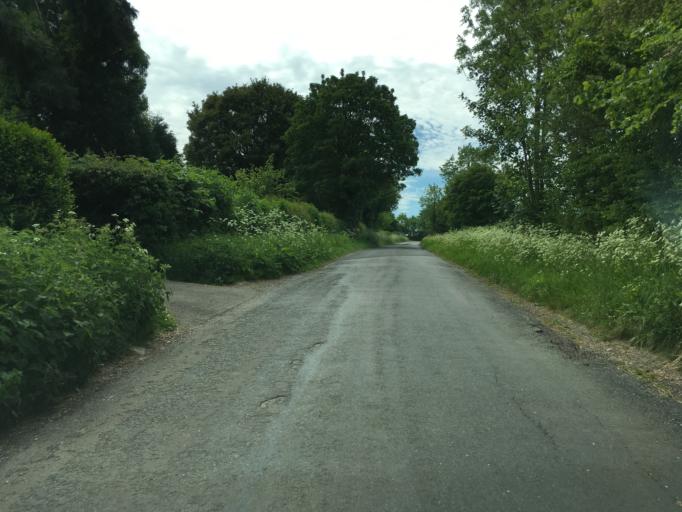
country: GB
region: England
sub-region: Gloucestershire
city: Dursley
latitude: 51.6684
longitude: -2.3859
